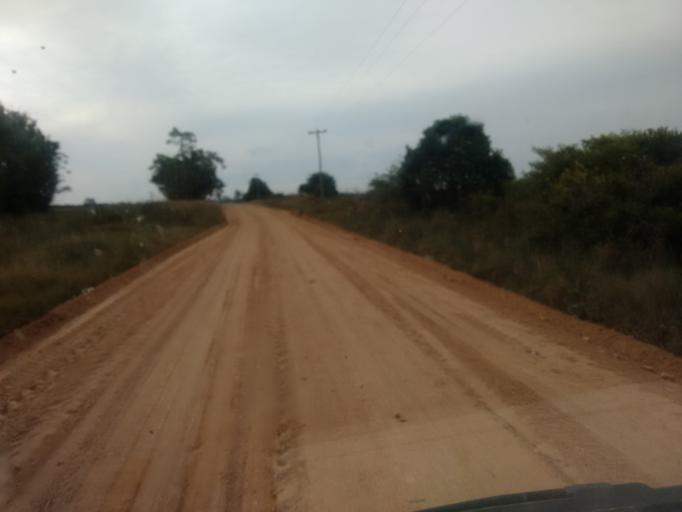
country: BR
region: Rio Grande do Sul
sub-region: Camaqua
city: Camaqua
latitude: -31.1398
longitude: -51.7648
